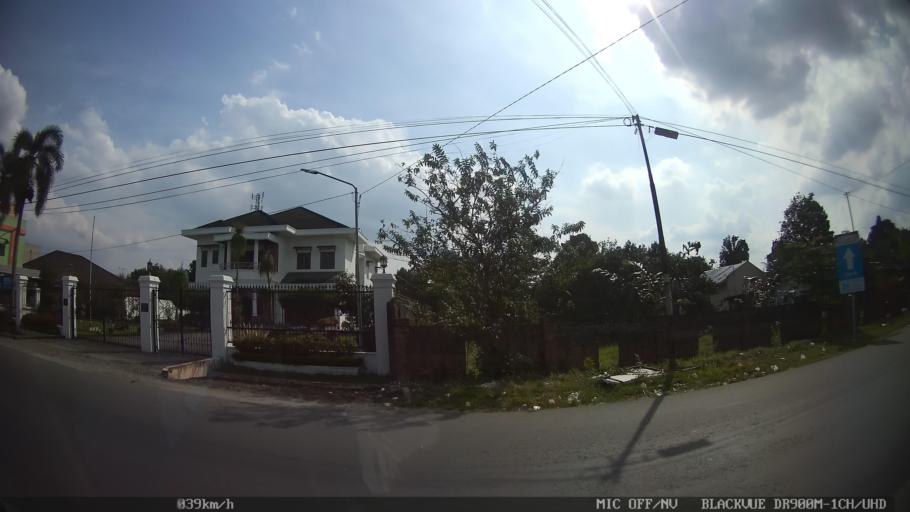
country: ID
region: North Sumatra
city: Binjai
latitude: 3.6324
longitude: 98.4904
